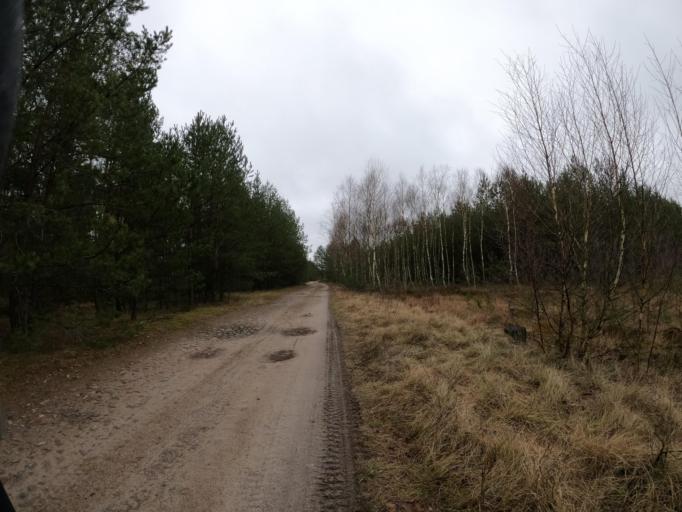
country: PL
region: Greater Poland Voivodeship
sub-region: Powiat zlotowski
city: Sypniewo
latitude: 53.5103
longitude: 16.5622
